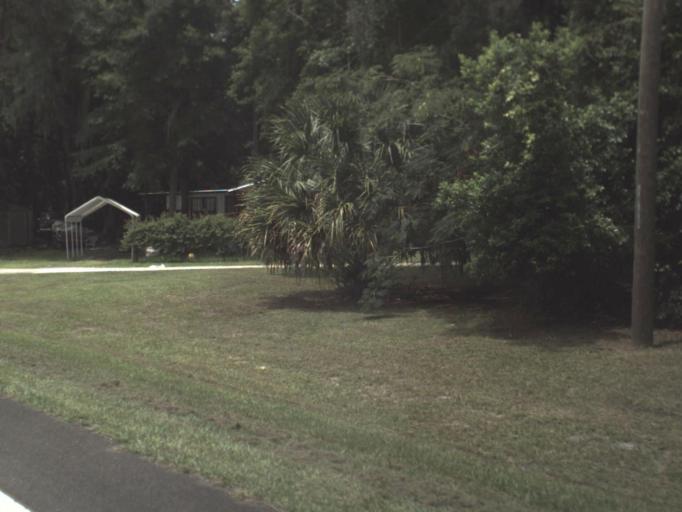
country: US
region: Florida
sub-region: Levy County
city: Williston
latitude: 29.4439
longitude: -82.4675
